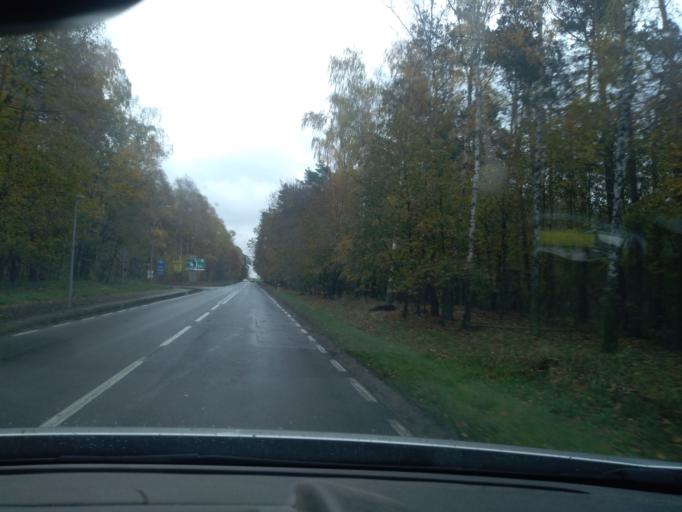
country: PL
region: Greater Poland Voivodeship
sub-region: Powiat obornicki
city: Oborniki
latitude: 52.6433
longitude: 16.8423
